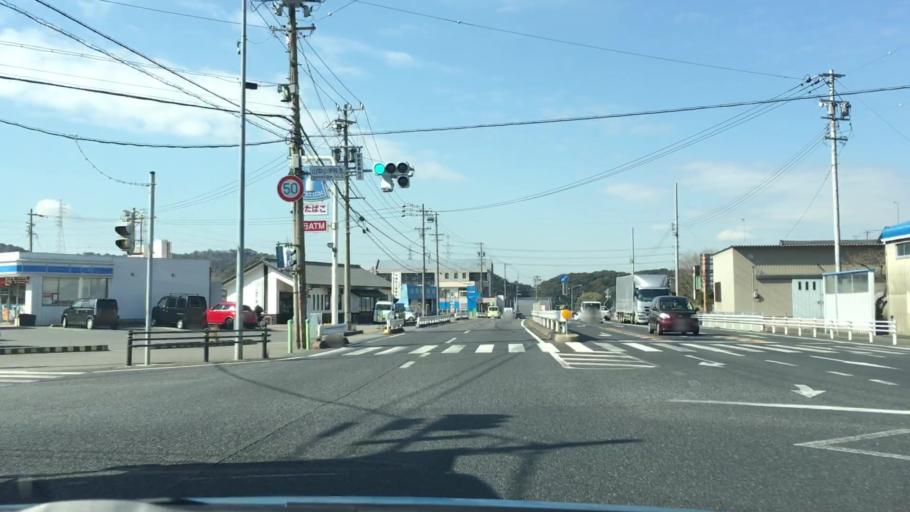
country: JP
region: Aichi
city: Gamagori
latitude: 34.8991
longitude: 137.2418
